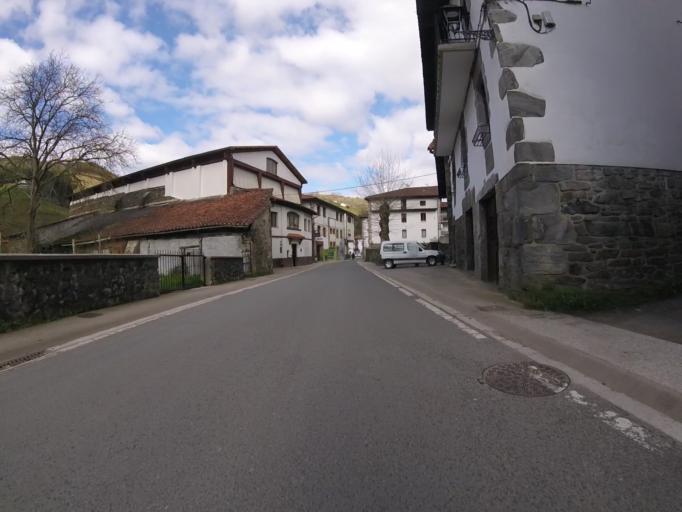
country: ES
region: Navarre
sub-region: Provincia de Navarra
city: Goizueta
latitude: 43.1704
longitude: -1.8633
